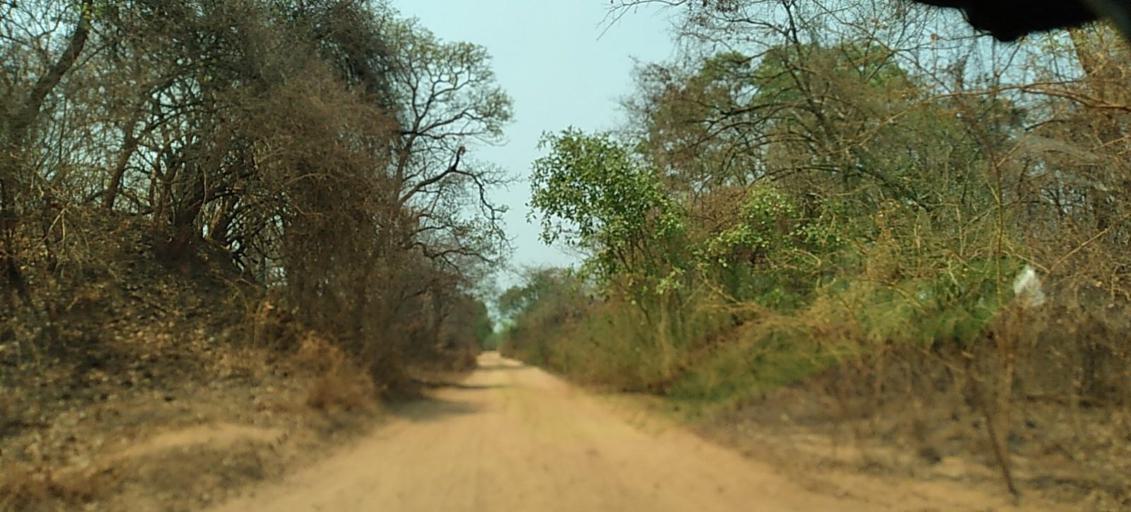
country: ZM
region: North-Western
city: Kabompo
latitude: -13.7022
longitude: 24.3189
